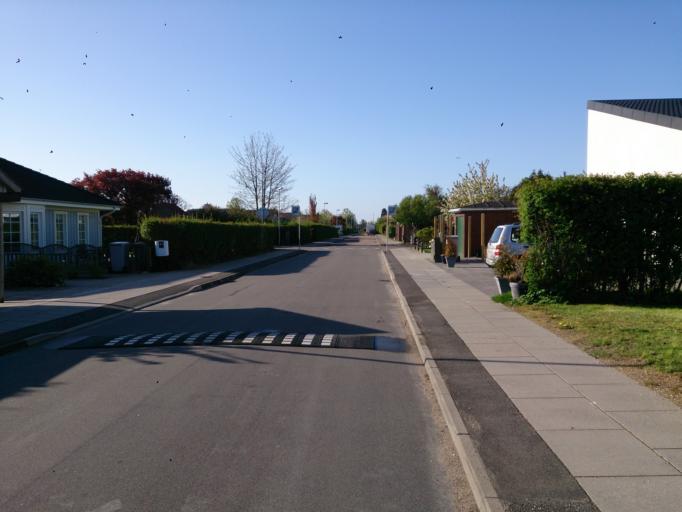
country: DK
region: Capital Region
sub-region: Tarnby Kommune
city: Tarnby
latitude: 55.6156
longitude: 12.5811
